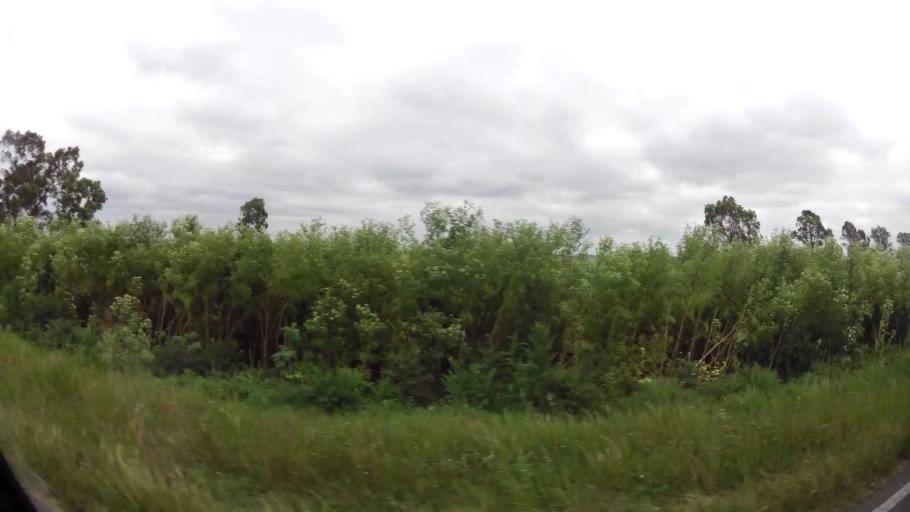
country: AR
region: Buenos Aires
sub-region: Partido de San Vicente
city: San Vicente
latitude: -35.0437
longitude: -58.4520
